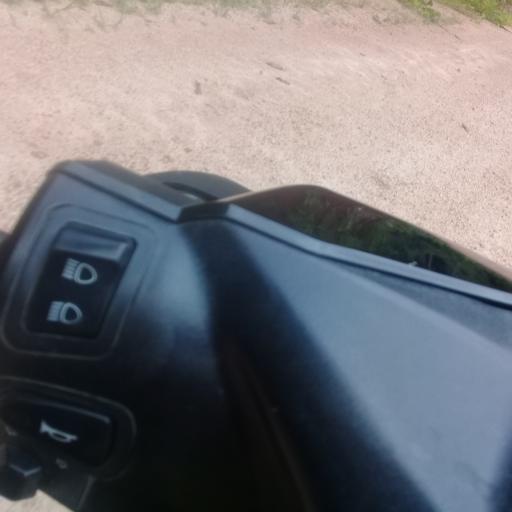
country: VN
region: Huyen Dien Bien
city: Thi Tran Muong Cha
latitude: 21.6683
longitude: 102.9147
